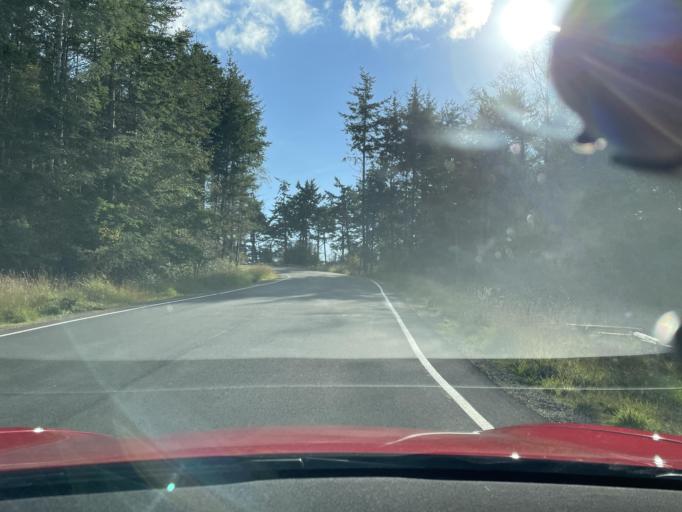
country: US
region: Washington
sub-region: San Juan County
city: Friday Harbor
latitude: 48.4654
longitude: -123.0259
